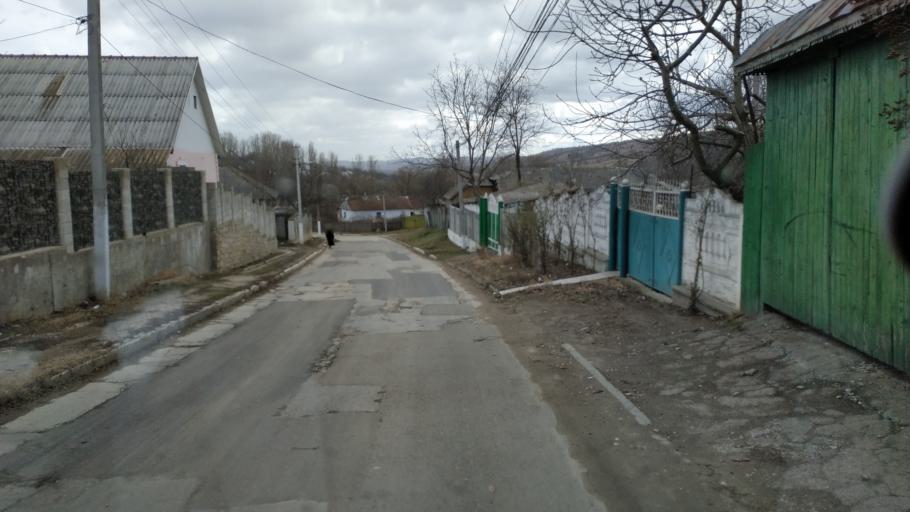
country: MD
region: Stinga Nistrului
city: Bucovat
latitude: 47.2322
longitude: 28.4238
